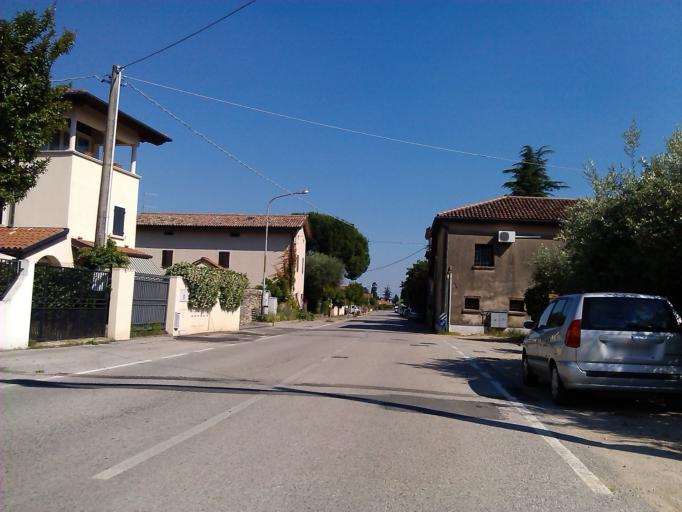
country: IT
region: Veneto
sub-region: Provincia di Vicenza
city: Pove del Grappa
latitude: 45.7928
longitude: 11.7291
